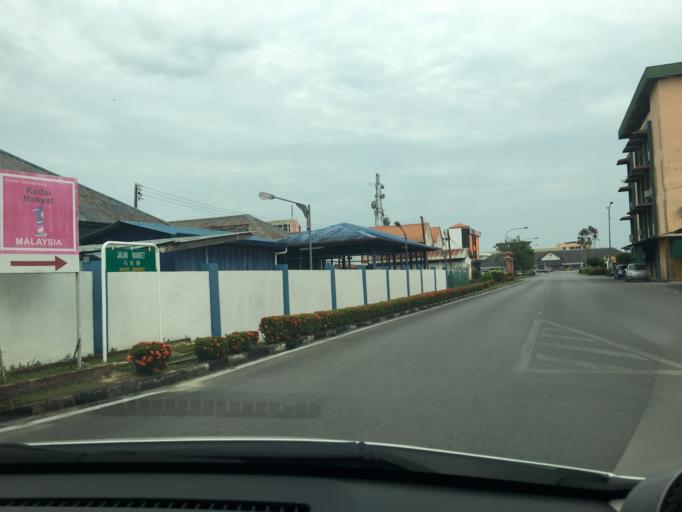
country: MY
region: Sarawak
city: Sarikei
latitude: 2.1334
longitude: 111.5224
